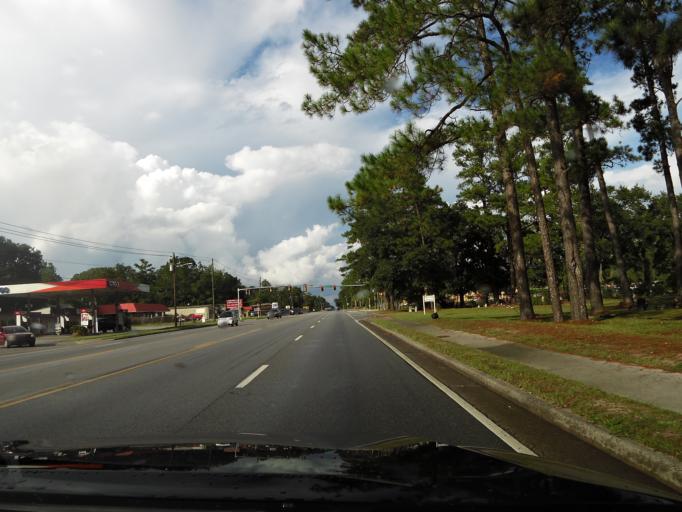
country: US
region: Georgia
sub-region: Liberty County
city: Walthourville
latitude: 31.7948
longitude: -81.6071
